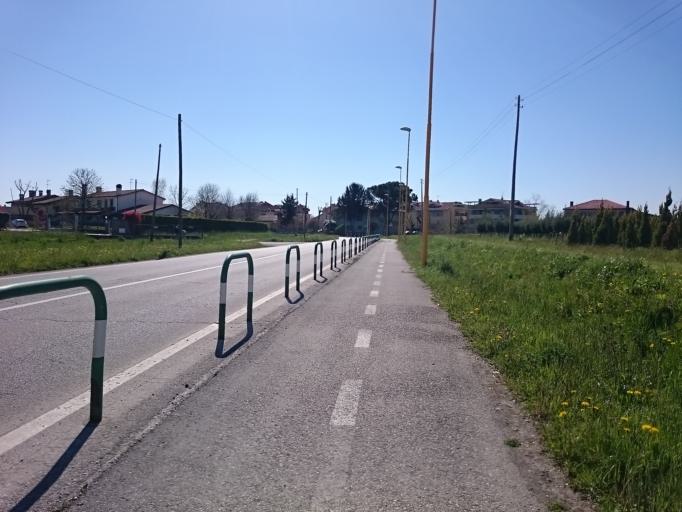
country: IT
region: Veneto
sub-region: Provincia di Padova
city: Ponte San Nicolo
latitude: 45.3680
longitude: 11.9071
